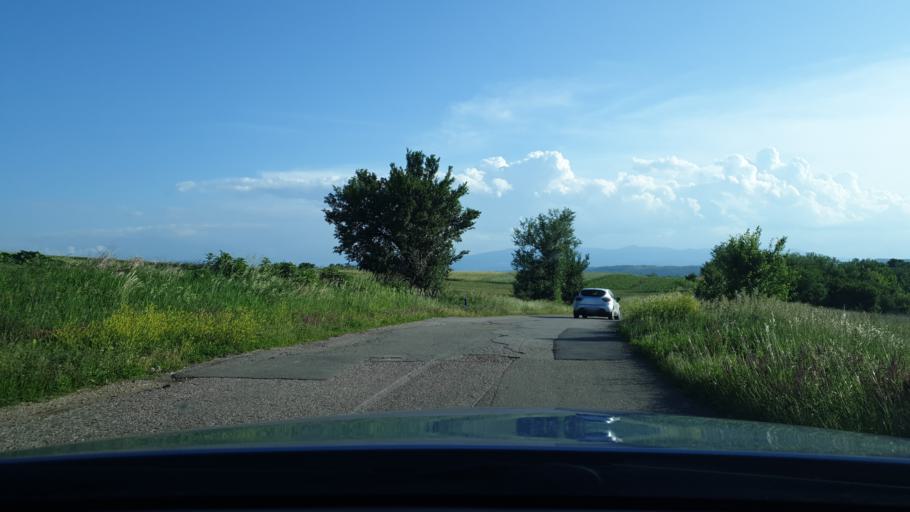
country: RS
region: Central Serbia
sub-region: Nisavski Okrug
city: Aleksinac
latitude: 43.6039
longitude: 21.6461
